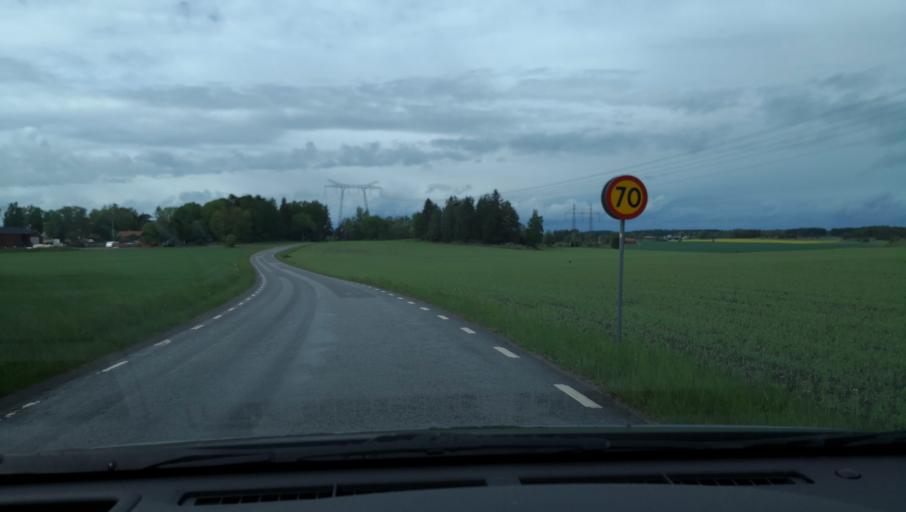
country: SE
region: Uppsala
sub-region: Enkopings Kommun
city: Orsundsbro
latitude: 59.6918
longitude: 17.3756
